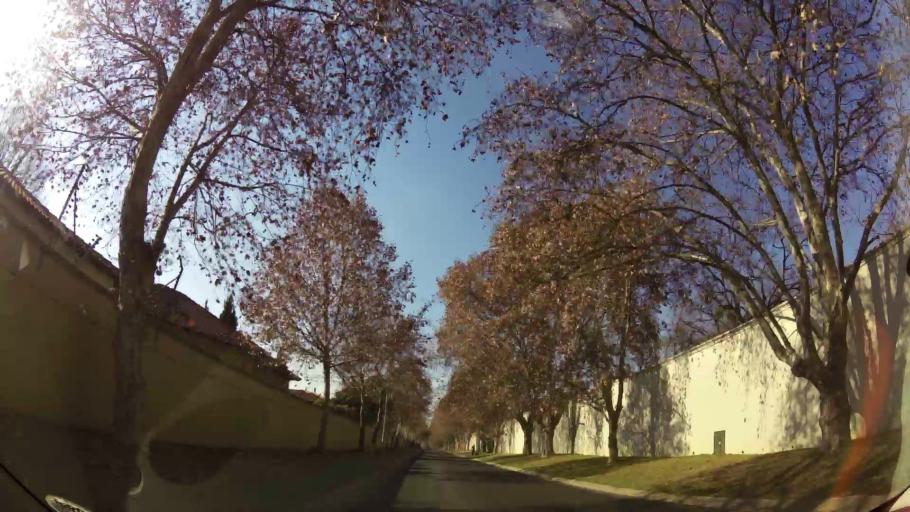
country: ZA
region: Gauteng
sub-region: City of Johannesburg Metropolitan Municipality
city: Diepsloot
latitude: -26.0661
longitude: 28.0019
